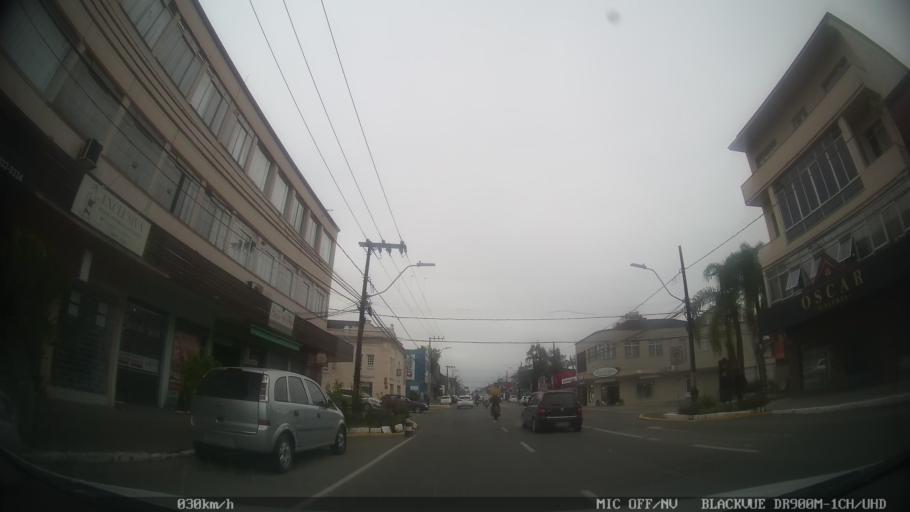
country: BR
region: Santa Catarina
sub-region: Joinville
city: Joinville
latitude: -26.3120
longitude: -48.8455
